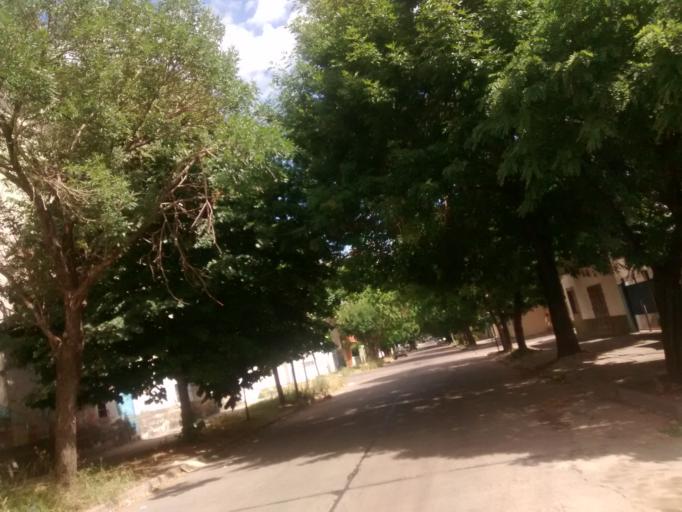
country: AR
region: Buenos Aires
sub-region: Partido de La Plata
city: La Plata
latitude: -34.9404
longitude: -57.9520
